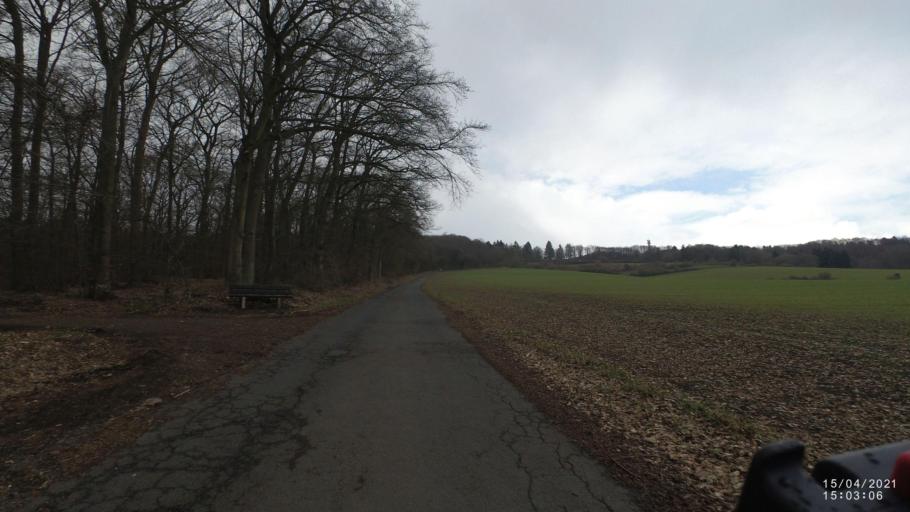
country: DE
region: Rheinland-Pfalz
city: Bell
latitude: 50.3911
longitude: 7.2160
